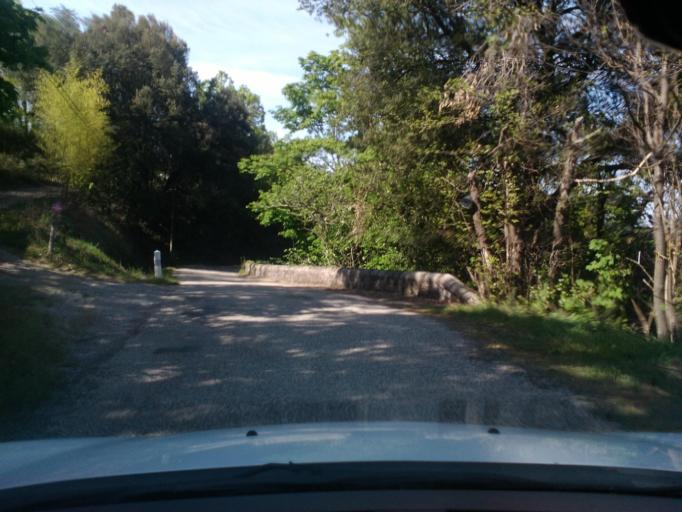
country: FR
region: Languedoc-Roussillon
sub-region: Departement du Gard
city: Lasalle
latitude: 44.0277
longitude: 3.8775
